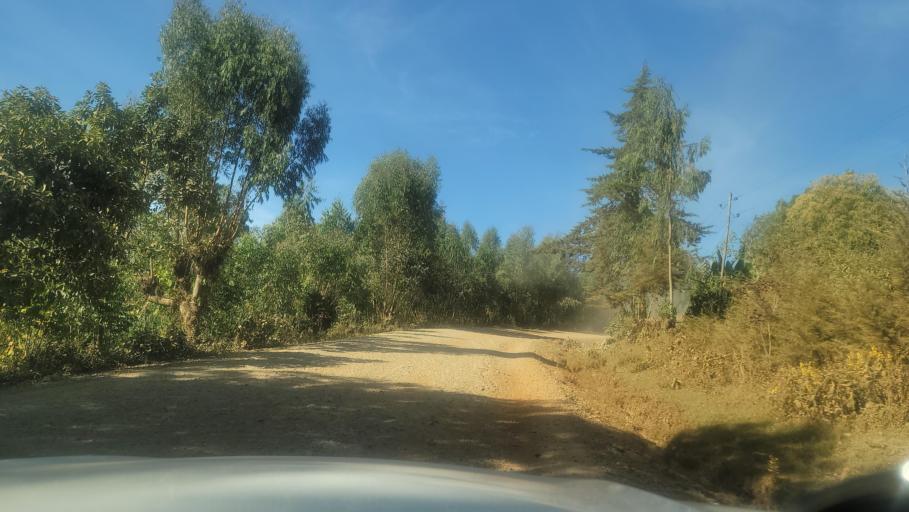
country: ET
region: Oromiya
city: Agaro
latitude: 7.8140
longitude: 36.5121
